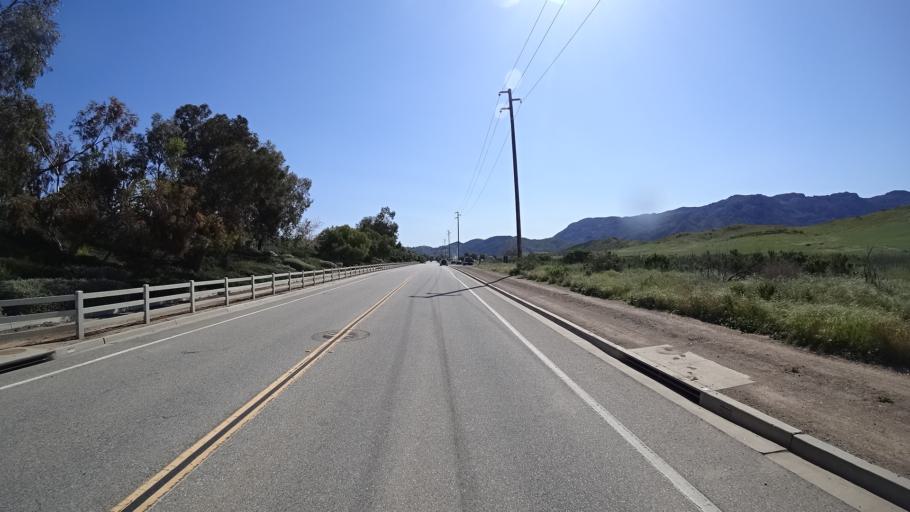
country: US
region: California
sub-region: Ventura County
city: Casa Conejo
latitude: 34.1563
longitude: -118.9873
